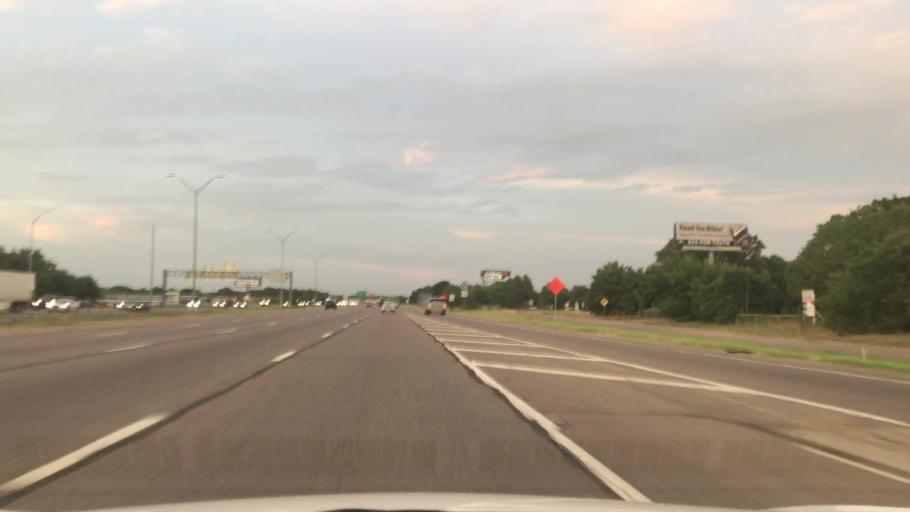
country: US
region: Texas
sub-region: Dallas County
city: Balch Springs
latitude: 32.7075
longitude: -96.6225
